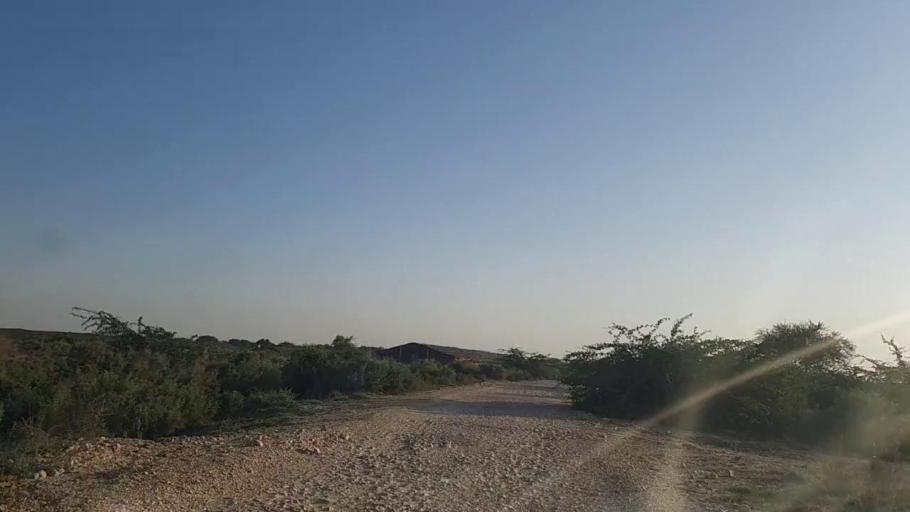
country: PK
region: Sindh
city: Jati
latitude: 24.4335
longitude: 68.1916
